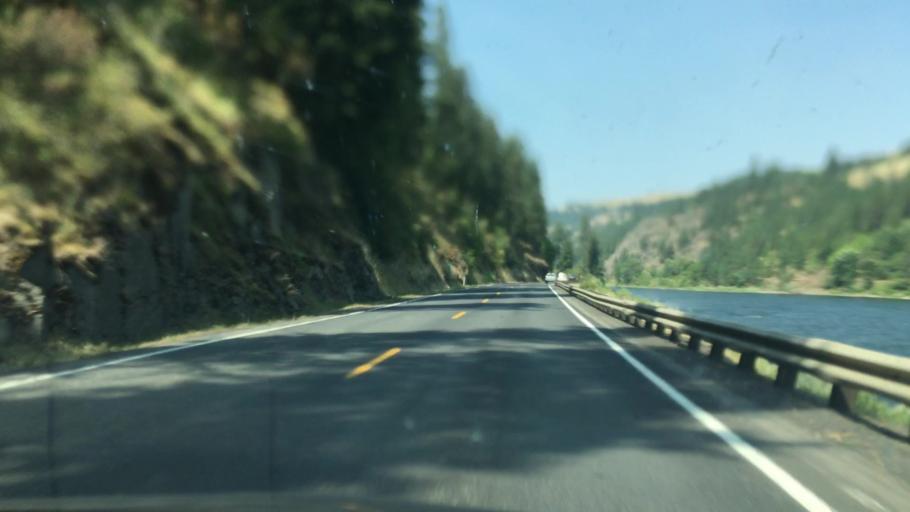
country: US
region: Idaho
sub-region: Clearwater County
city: Orofino
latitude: 46.4966
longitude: -116.4108
